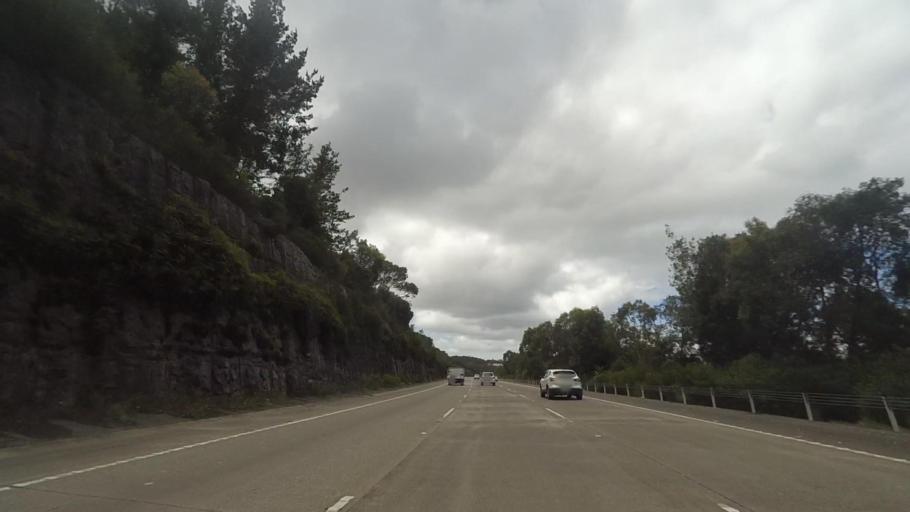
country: AU
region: New South Wales
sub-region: Gosford Shire
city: Point Clare
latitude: -33.4320
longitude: 151.2711
